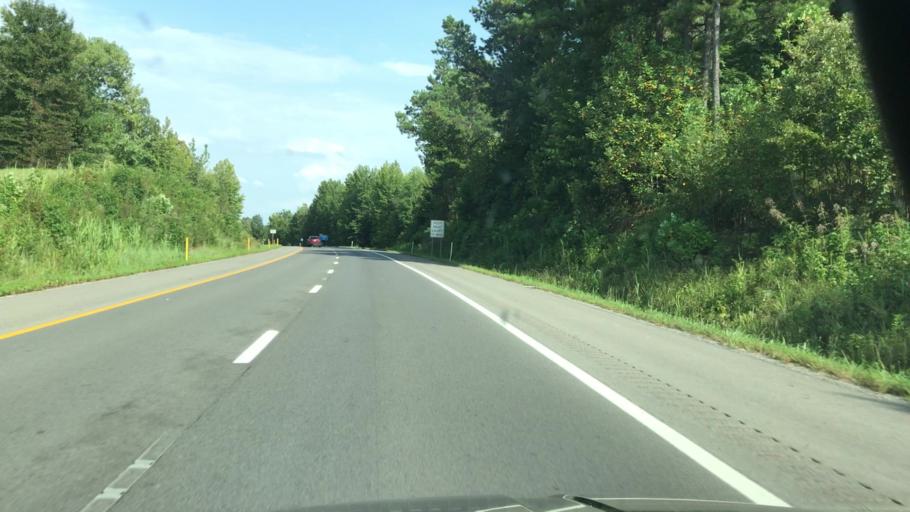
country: US
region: Kentucky
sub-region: Hopkins County
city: Nortonville
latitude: 37.2110
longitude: -87.4227
